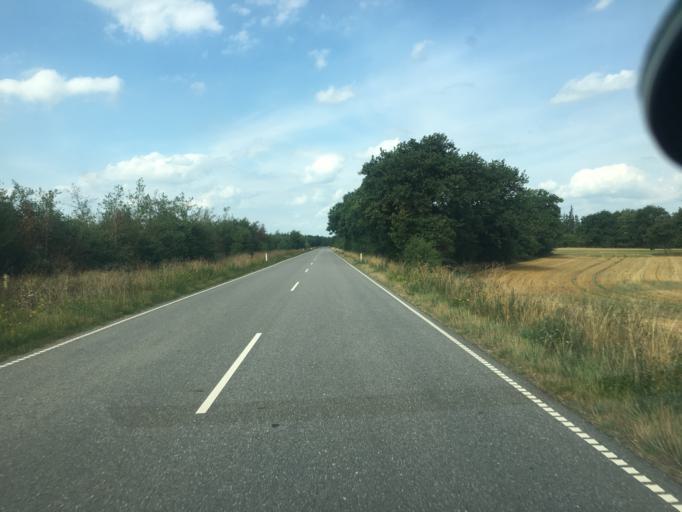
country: DK
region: South Denmark
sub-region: Aabenraa Kommune
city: Tinglev
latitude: 54.9382
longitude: 9.3085
